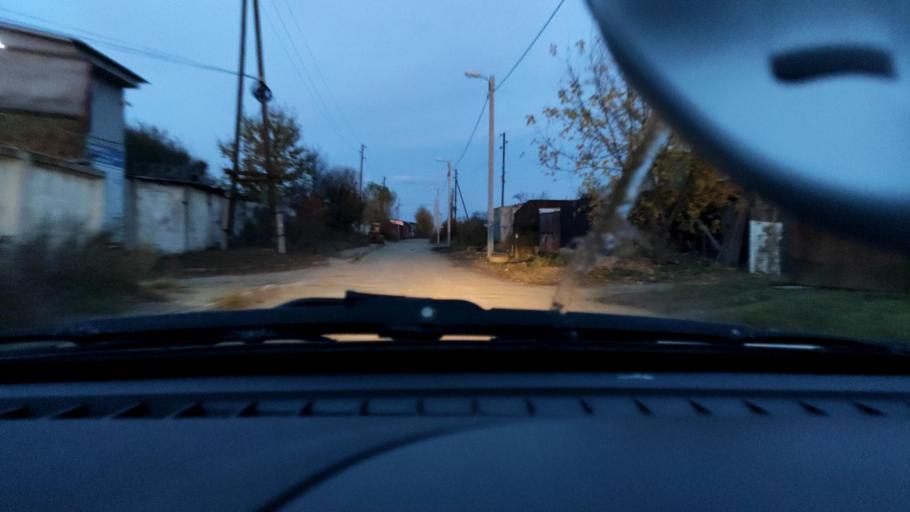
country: RU
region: Perm
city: Kondratovo
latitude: 58.0059
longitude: 56.0896
